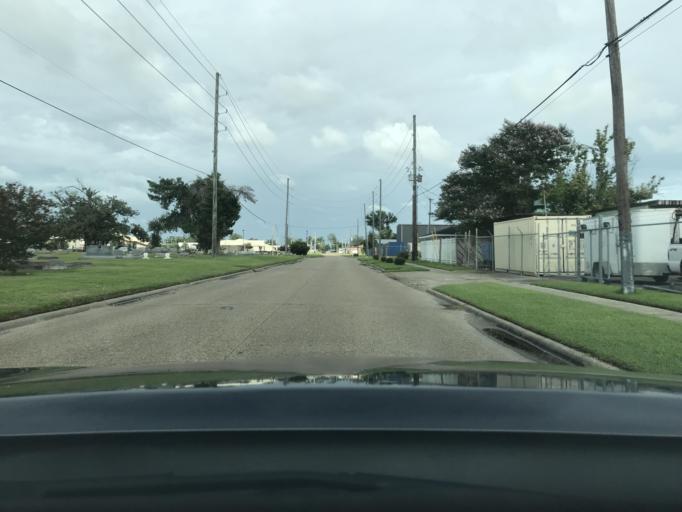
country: US
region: Louisiana
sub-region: Calcasieu Parish
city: Westlake
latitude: 30.2477
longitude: -93.2622
